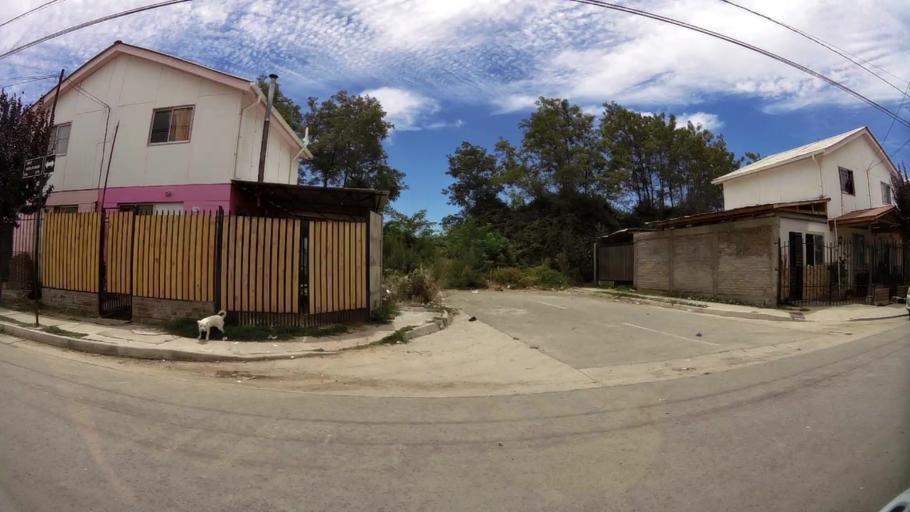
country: CL
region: O'Higgins
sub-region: Provincia de Cachapoal
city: Graneros
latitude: -34.0722
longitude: -70.7394
